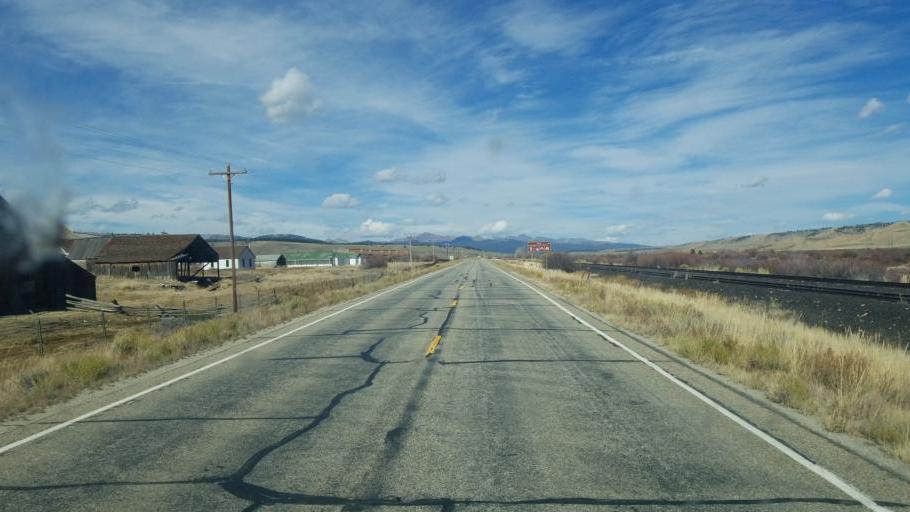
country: US
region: Colorado
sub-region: Lake County
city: Leadville
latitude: 39.1260
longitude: -106.3136
